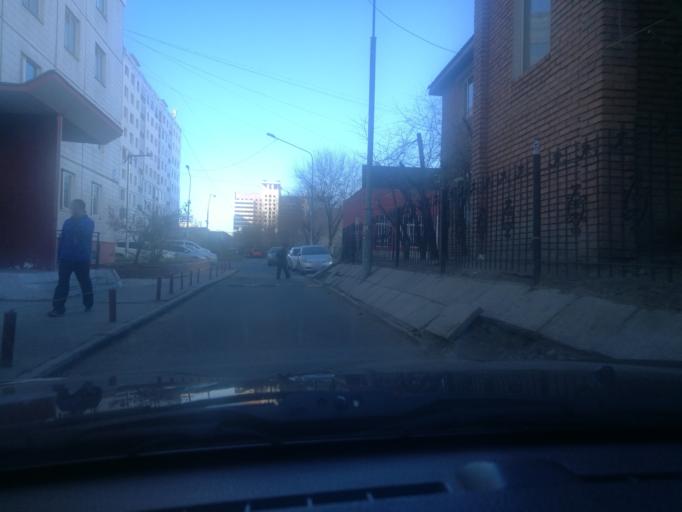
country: MN
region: Ulaanbaatar
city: Ulaanbaatar
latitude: 47.9135
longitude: 106.9105
